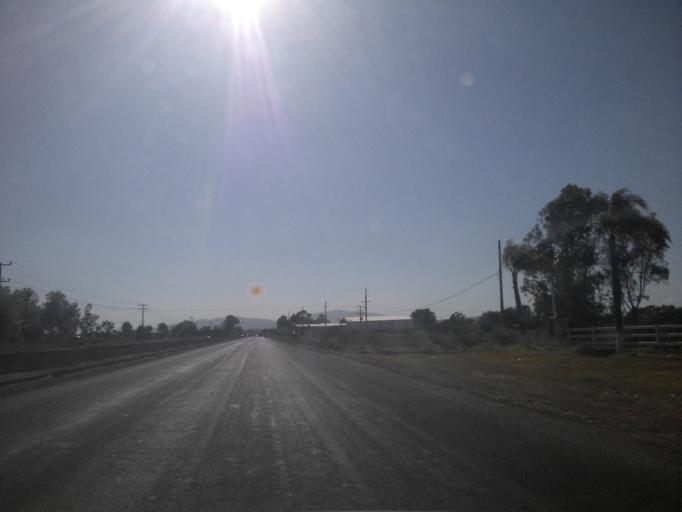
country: MX
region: Jalisco
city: Arandas
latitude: 20.7089
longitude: -102.3916
